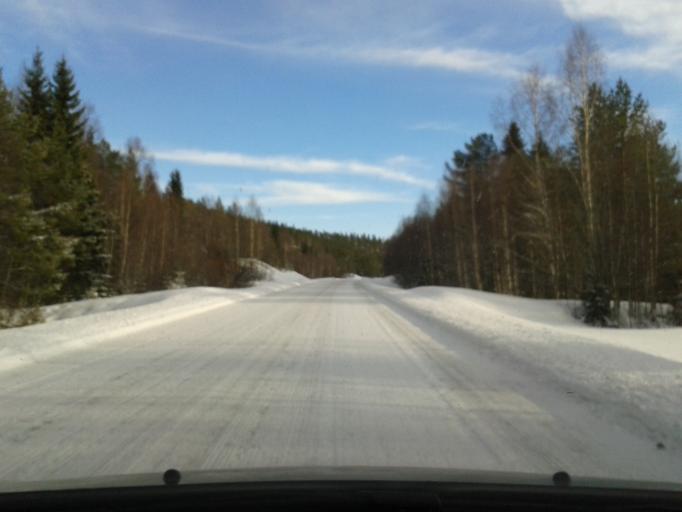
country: SE
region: Vaesterbotten
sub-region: Asele Kommun
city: Asele
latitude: 64.3211
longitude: 17.1087
